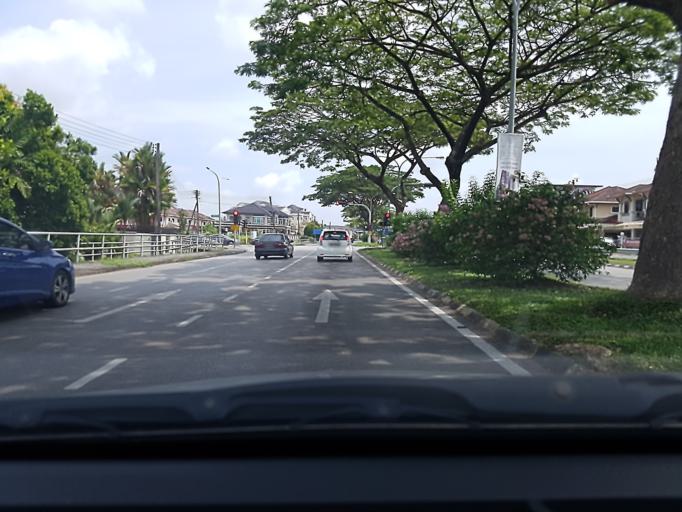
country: MY
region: Sarawak
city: Kuching
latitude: 1.5178
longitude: 110.3638
